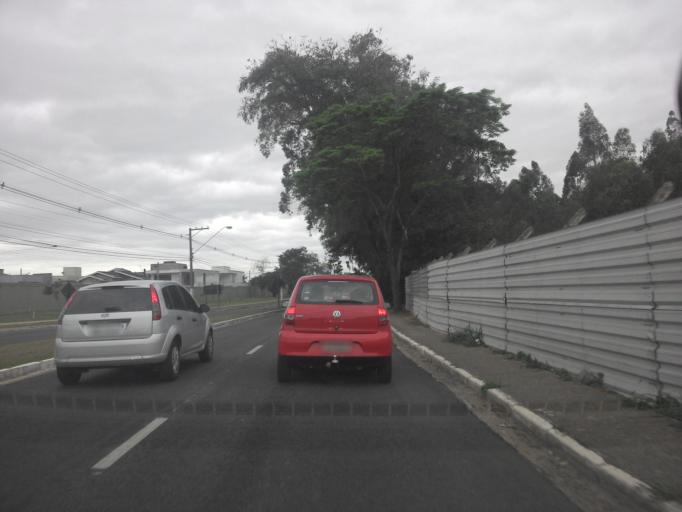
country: BR
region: Sao Paulo
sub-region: Taubate
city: Taubate
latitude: -23.0273
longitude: -45.6018
